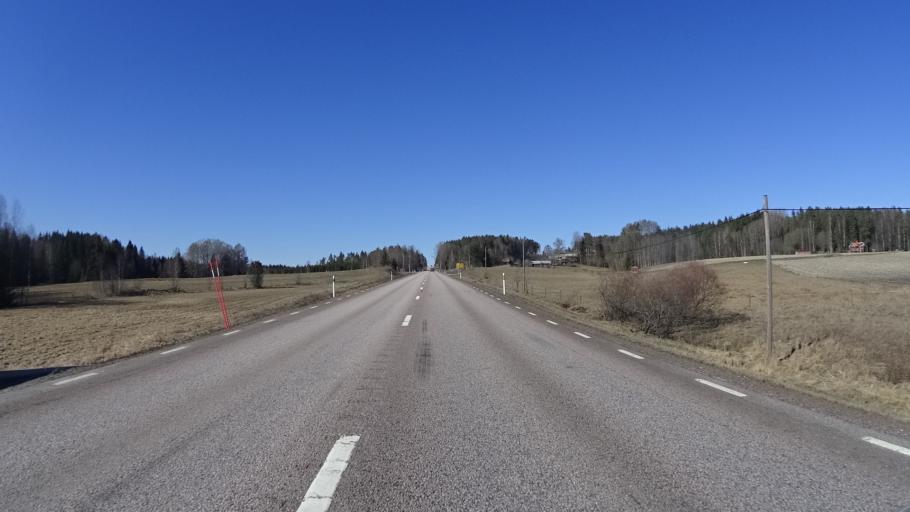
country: SE
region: Vaermland
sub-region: Karlstads Kommun
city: Edsvalla
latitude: 59.5784
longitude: 13.0182
